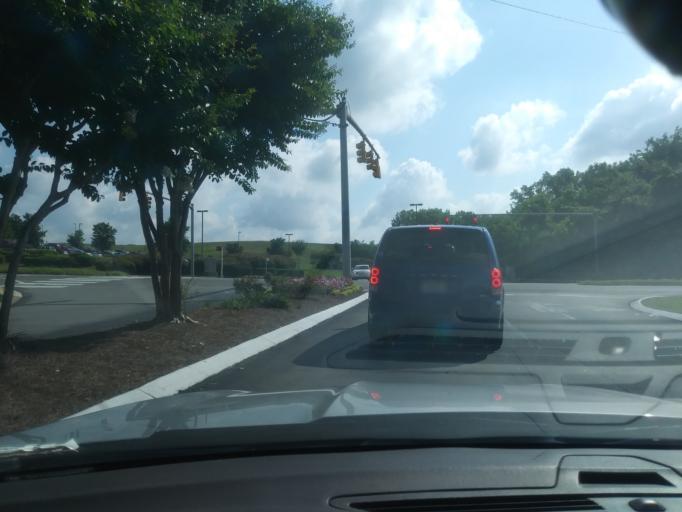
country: US
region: Tennessee
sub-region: Davidson County
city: Nashville
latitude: 36.1358
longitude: -86.6991
